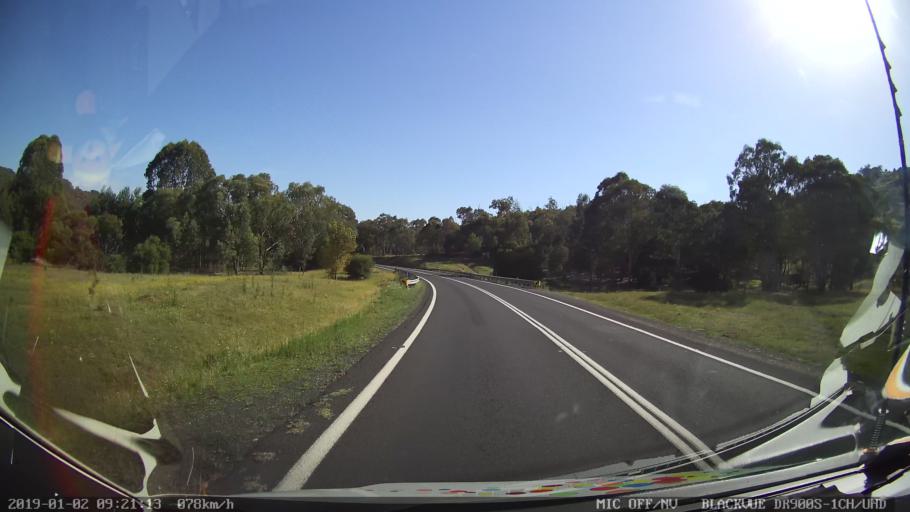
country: AU
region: New South Wales
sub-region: Tumut Shire
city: Tumut
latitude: -35.4083
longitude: 148.2907
